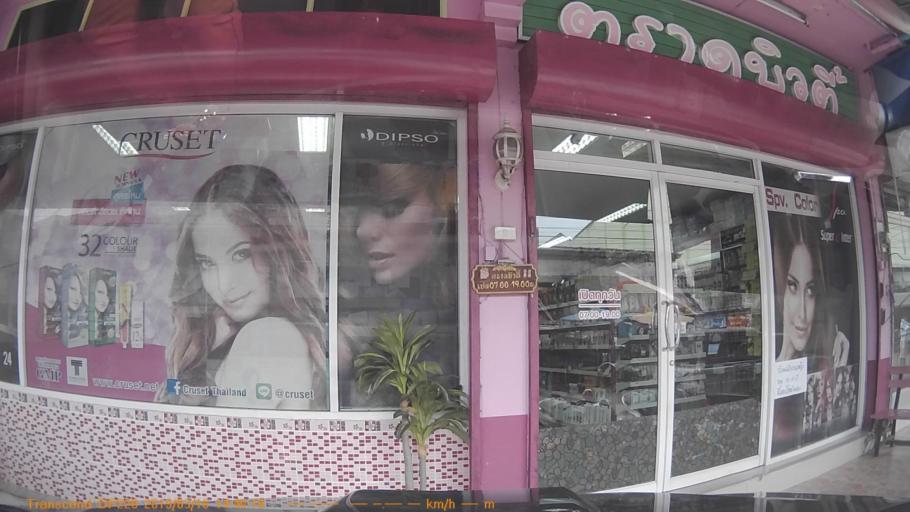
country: TH
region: Trat
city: Trat
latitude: 12.2455
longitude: 102.5119
